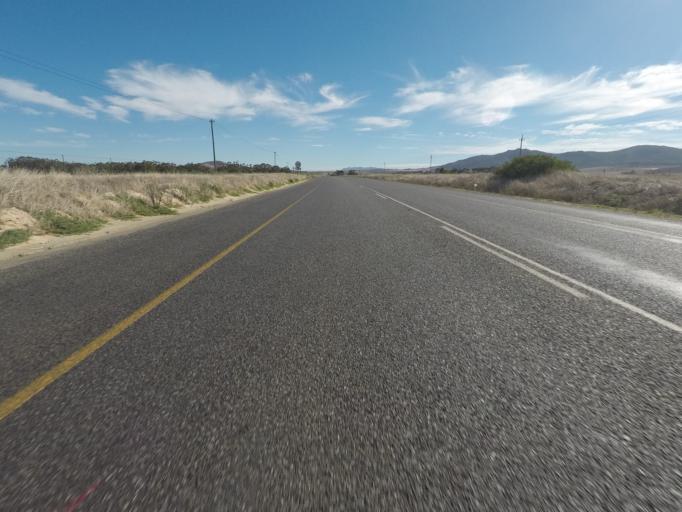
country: ZA
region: Western Cape
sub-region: West Coast District Municipality
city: Malmesbury
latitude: -33.6214
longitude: 18.7257
